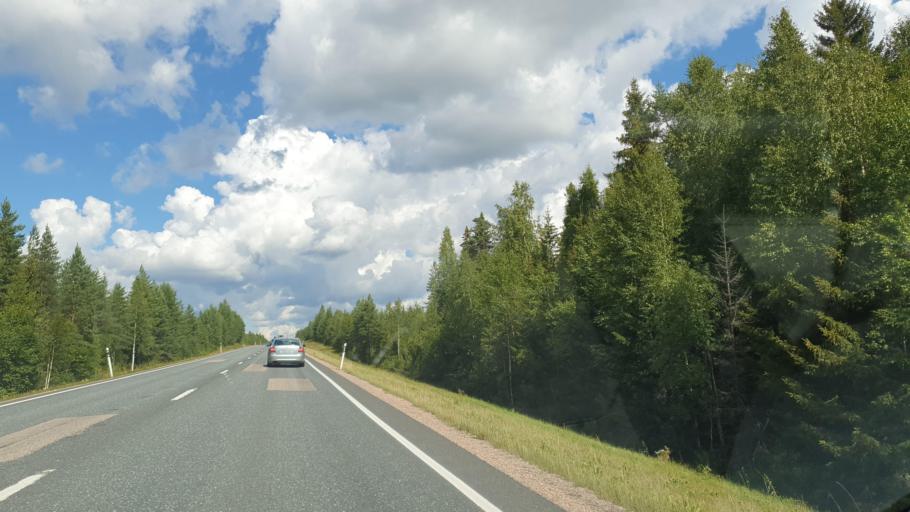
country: FI
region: Kainuu
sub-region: Kajaani
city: Kajaani
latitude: 64.0329
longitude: 27.4469
